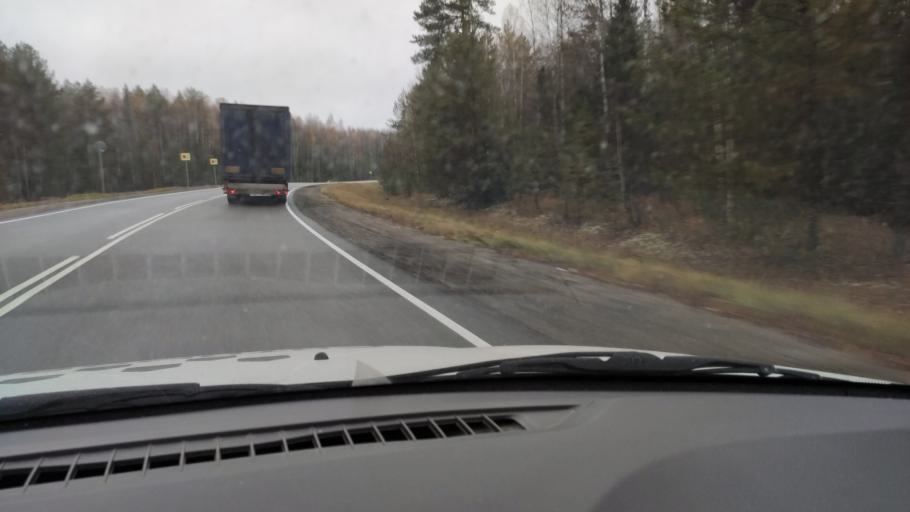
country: RU
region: Kirov
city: Chernaya Kholunitsa
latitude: 58.8299
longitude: 51.7638
